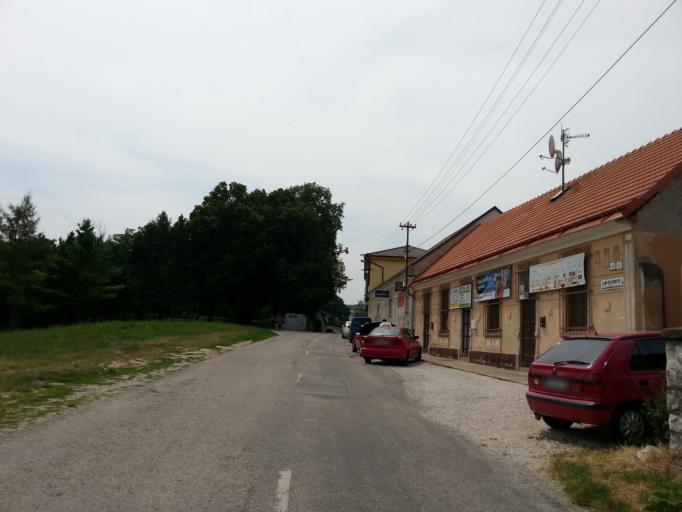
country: SK
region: Trenciansky
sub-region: Okres Nove Mesto nad Vahom
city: Nove Mesto nad Vahom
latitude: 48.7549
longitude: 17.8288
